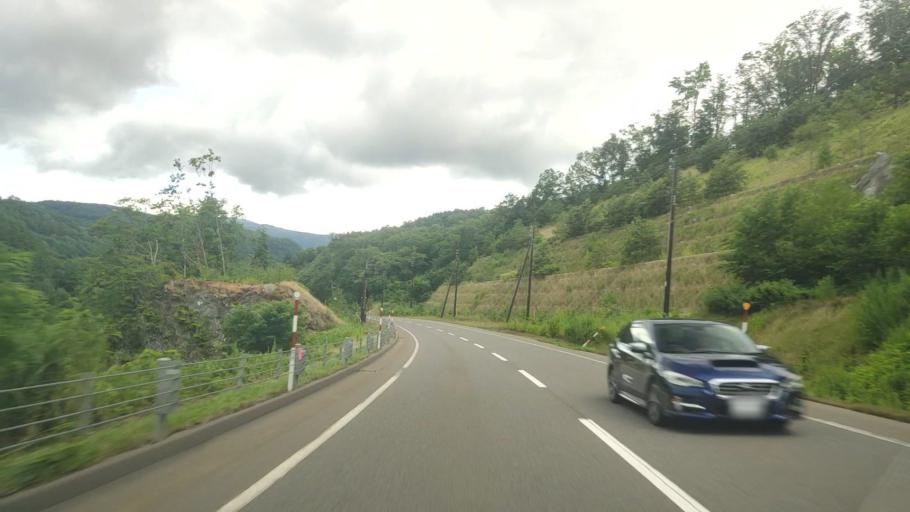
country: JP
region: Hokkaido
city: Date
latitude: 42.6054
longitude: 141.0244
